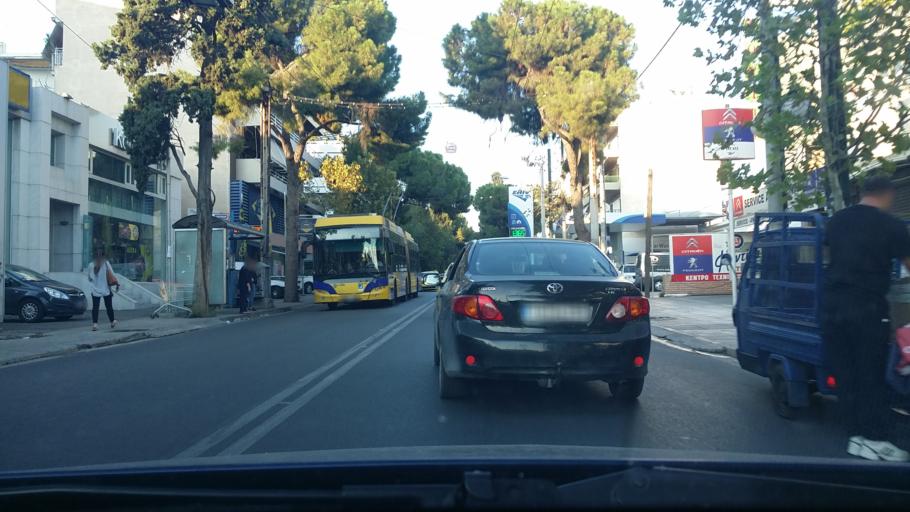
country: GR
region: Attica
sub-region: Nomarchia Athinas
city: Nea Chalkidona
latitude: 38.0277
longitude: 23.7327
